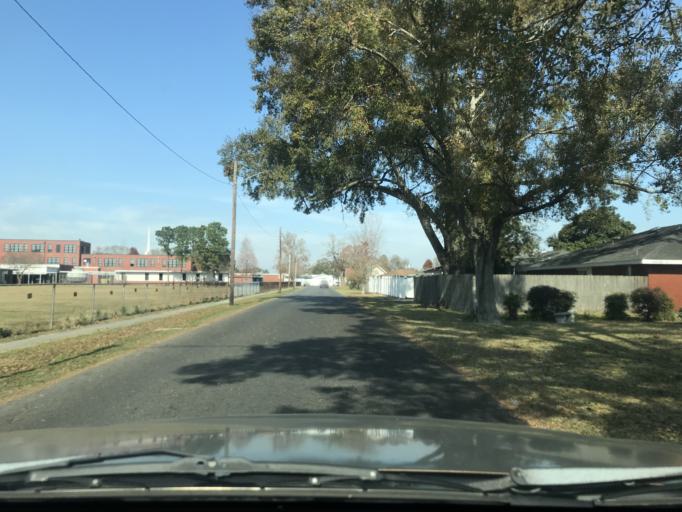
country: US
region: Louisiana
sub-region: Jefferson Parish
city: Marrero
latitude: 29.8980
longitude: -90.0901
